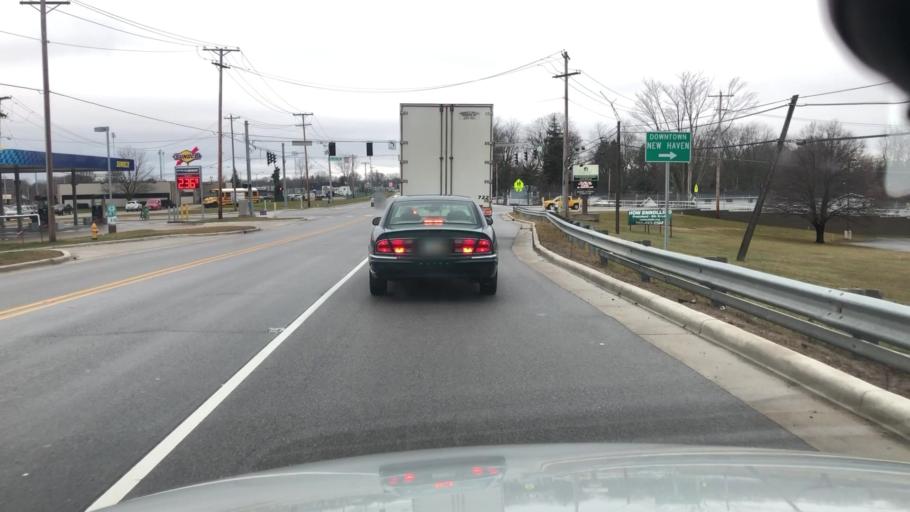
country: US
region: Indiana
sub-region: Allen County
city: New Haven
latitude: 41.0669
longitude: -85.0097
